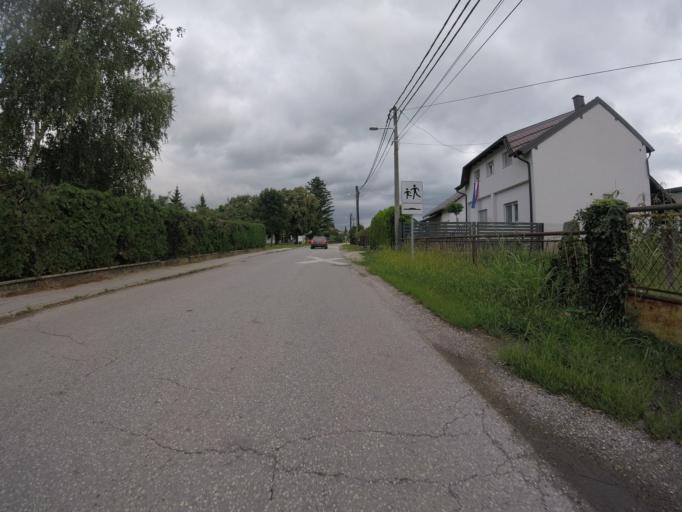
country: HR
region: Zagrebacka
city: Gradici
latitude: 45.7029
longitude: 16.0370
